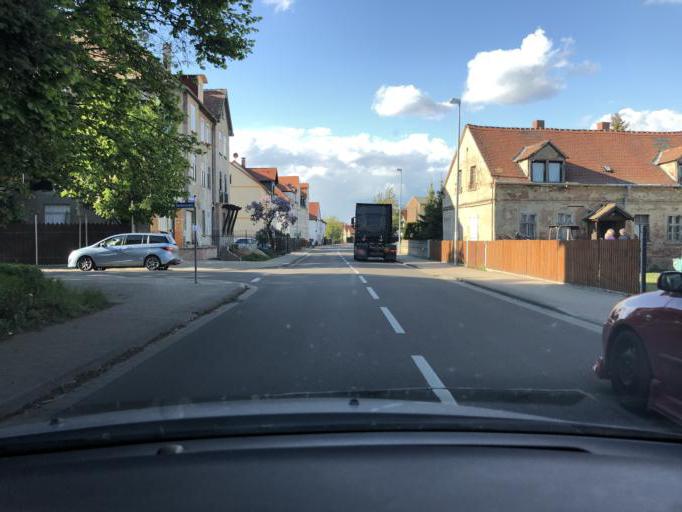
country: DE
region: Saxony
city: Bohlen
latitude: 51.2360
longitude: 12.3850
